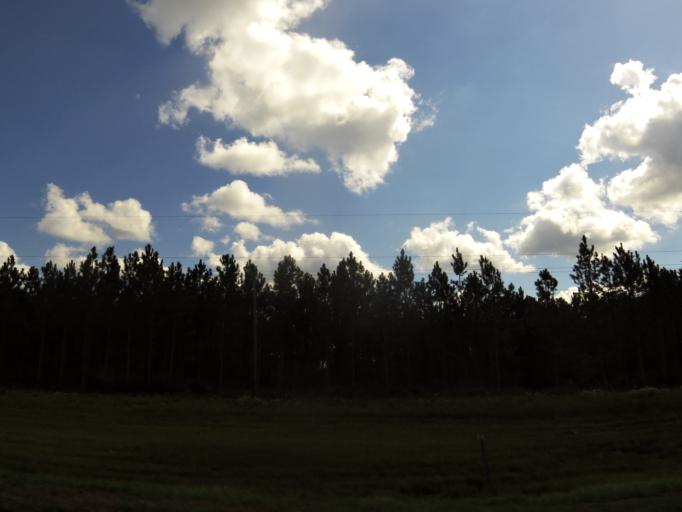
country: US
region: Florida
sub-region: Hamilton County
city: Jasper
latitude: 30.6744
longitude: -82.6442
